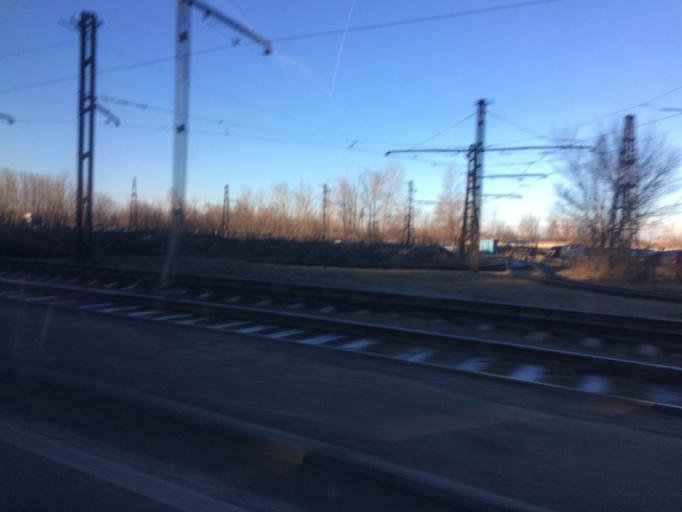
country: RU
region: Chelyabinsk
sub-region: Gorod Magnitogorsk
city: Magnitogorsk
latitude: 53.4109
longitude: 59.0324
